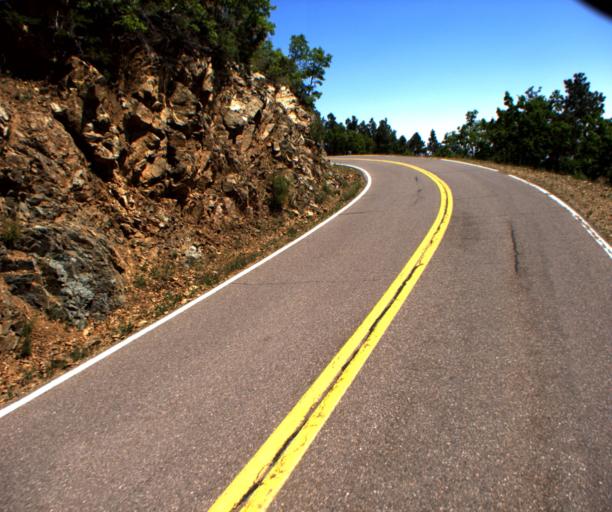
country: US
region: Arizona
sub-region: Graham County
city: Swift Trail Junction
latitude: 32.6361
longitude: -109.8485
